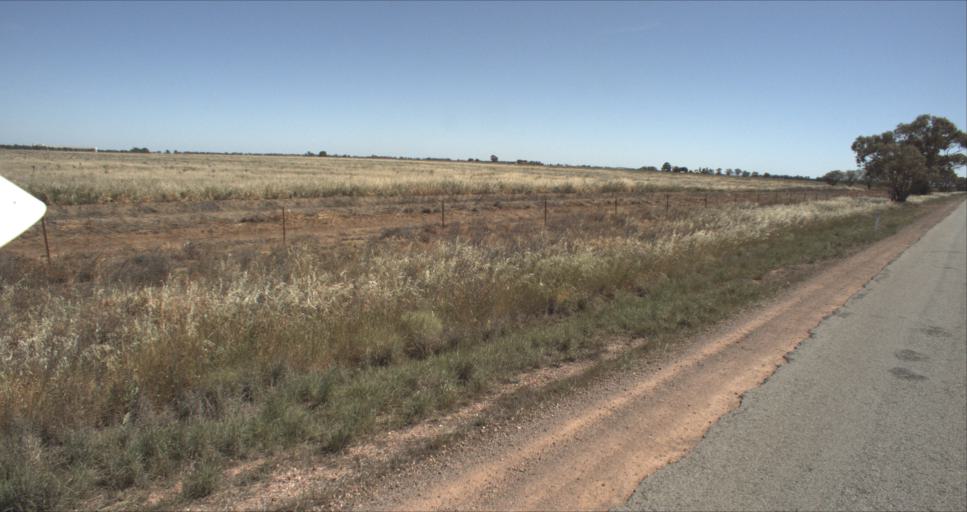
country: AU
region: New South Wales
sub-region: Leeton
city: Leeton
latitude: -34.5621
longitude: 146.3125
